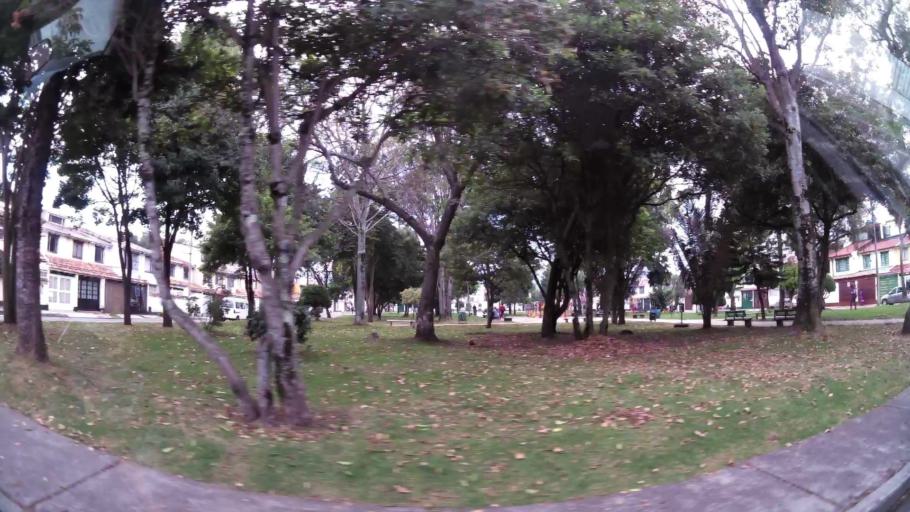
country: CO
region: Cundinamarca
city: Cota
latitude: 4.7542
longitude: -74.0488
